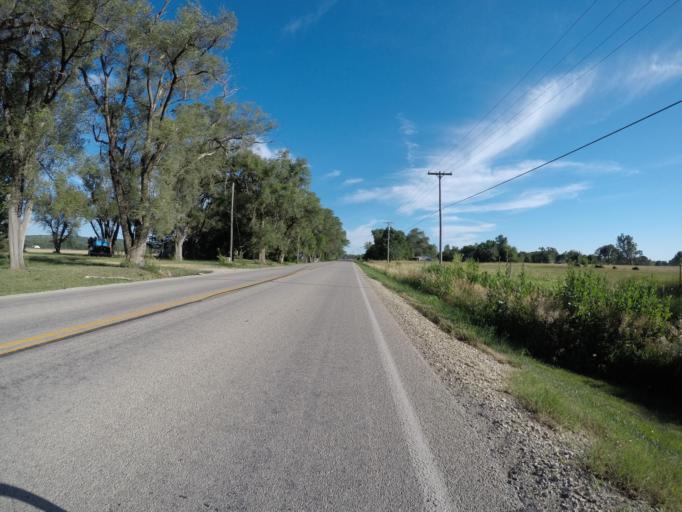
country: US
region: Kansas
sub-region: Riley County
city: Manhattan
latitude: 39.1625
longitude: -96.5771
